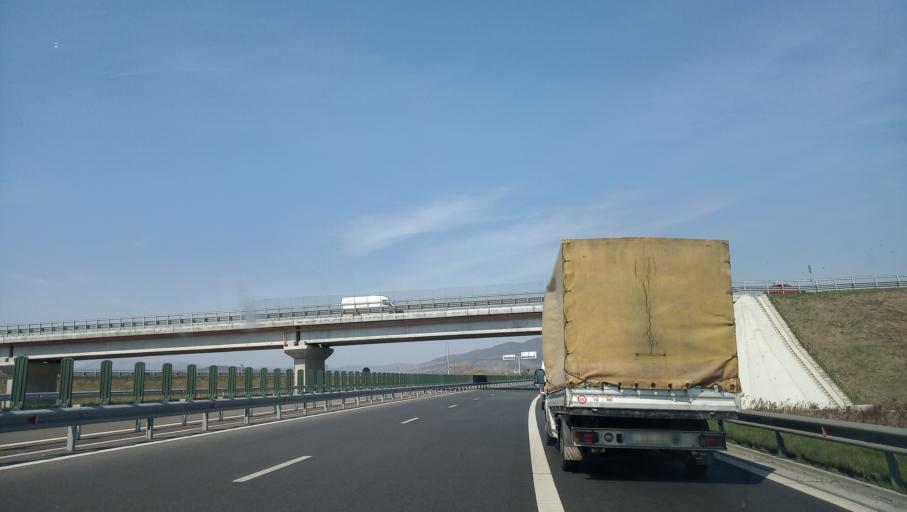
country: RO
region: Alba
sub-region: Municipiul Aiud
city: Aiud
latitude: 46.3288
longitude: 23.7294
